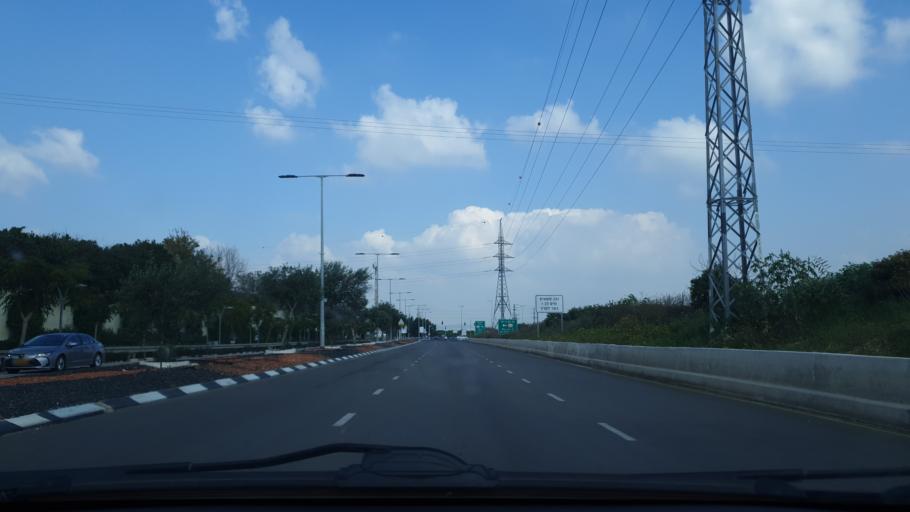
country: IL
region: Central District
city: Kefar Habad
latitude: 31.9725
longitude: 34.8371
